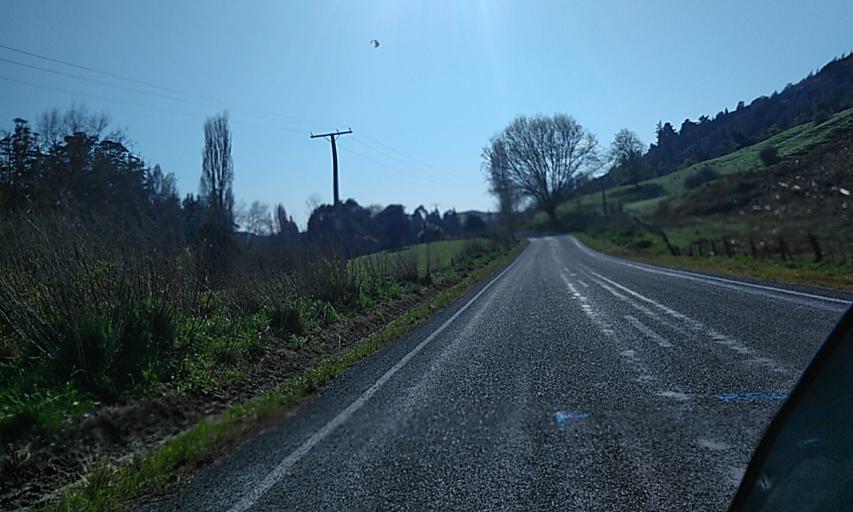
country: NZ
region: Gisborne
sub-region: Gisborne District
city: Gisborne
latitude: -38.5163
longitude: 178.0379
